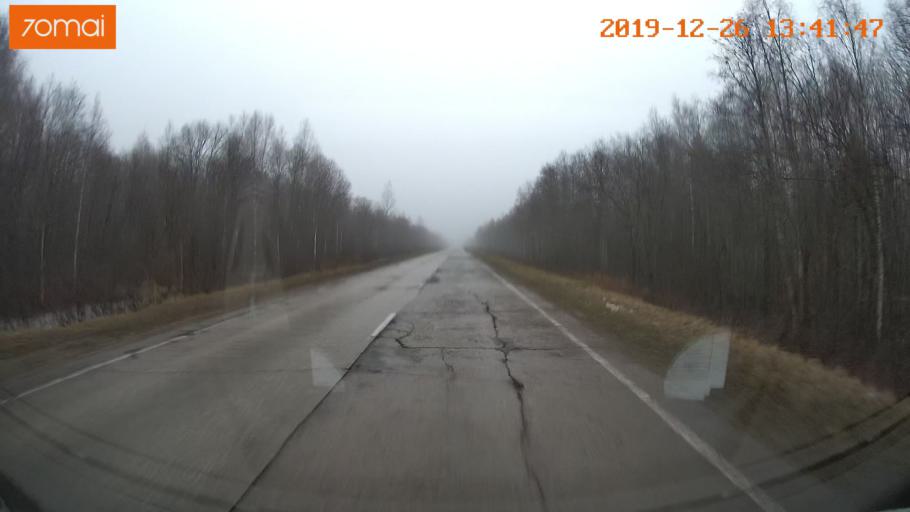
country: RU
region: Vologda
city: Sheksna
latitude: 58.7279
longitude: 38.4555
